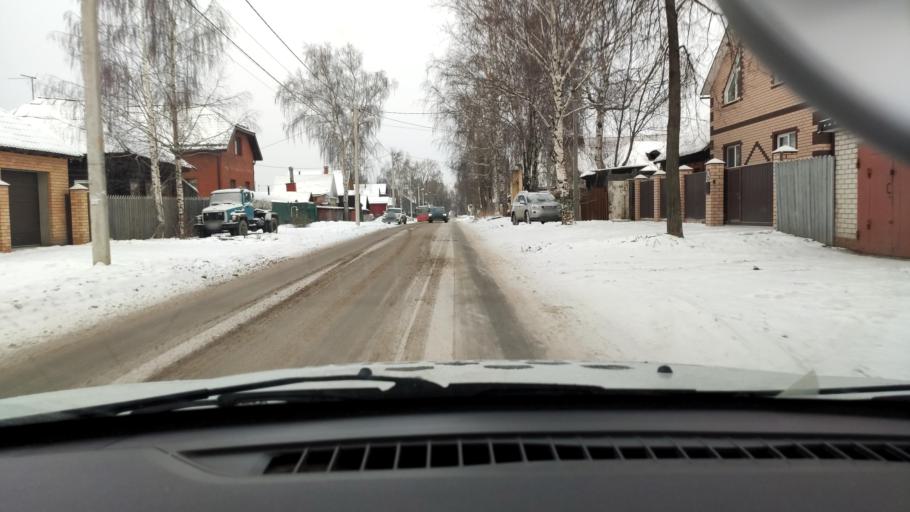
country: RU
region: Perm
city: Polazna
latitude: 58.1220
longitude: 56.3957
